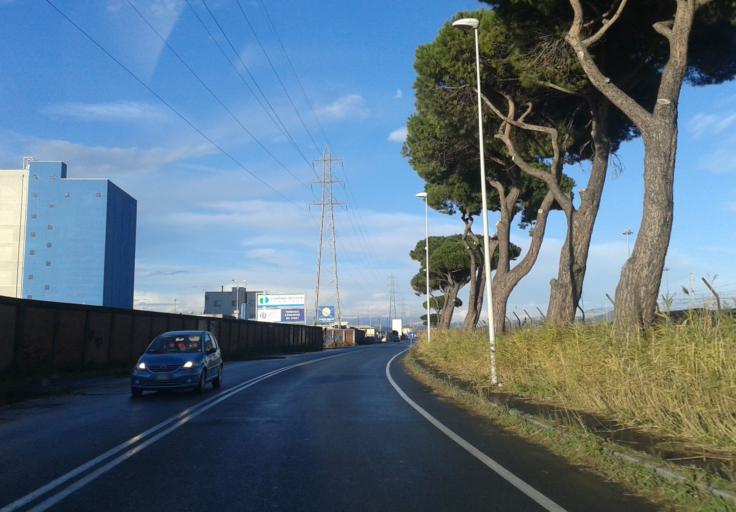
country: IT
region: Tuscany
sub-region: Provincia di Livorno
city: Livorno
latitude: 43.5770
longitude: 10.3213
